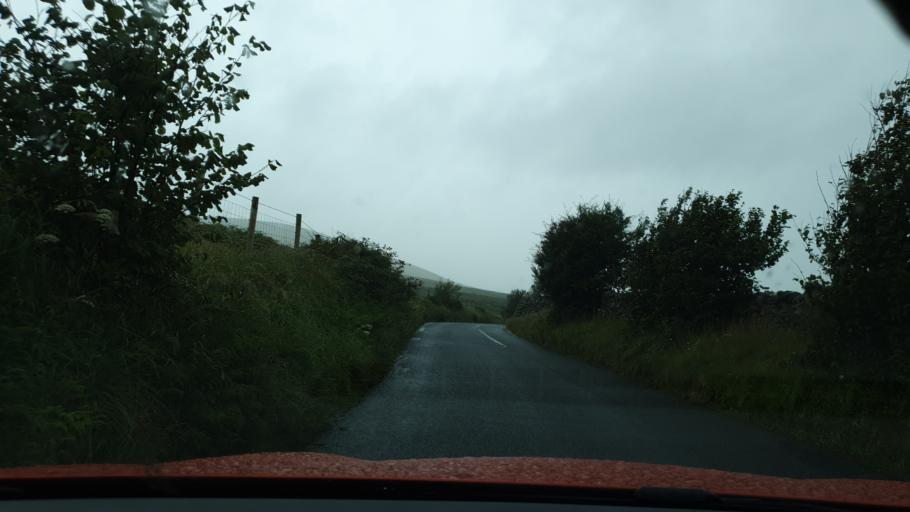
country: GB
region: England
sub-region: Cumbria
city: Millom
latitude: 54.3351
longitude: -3.2390
